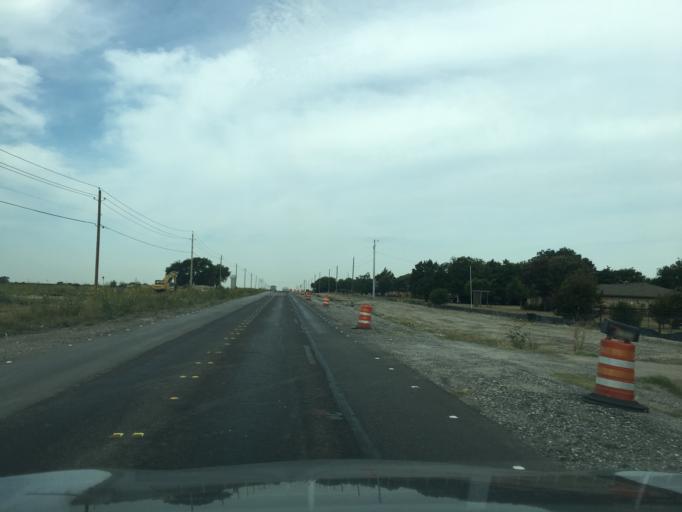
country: US
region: Texas
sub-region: Collin County
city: Parker
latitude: 33.0553
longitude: -96.6031
